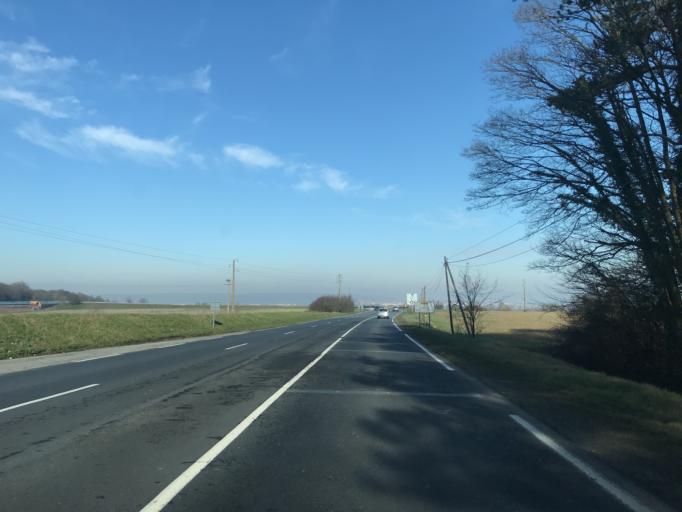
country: FR
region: Haute-Normandie
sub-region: Departement de l'Eure
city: Saint-Pierre-du-Vauvray
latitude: 49.2232
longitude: 1.2129
